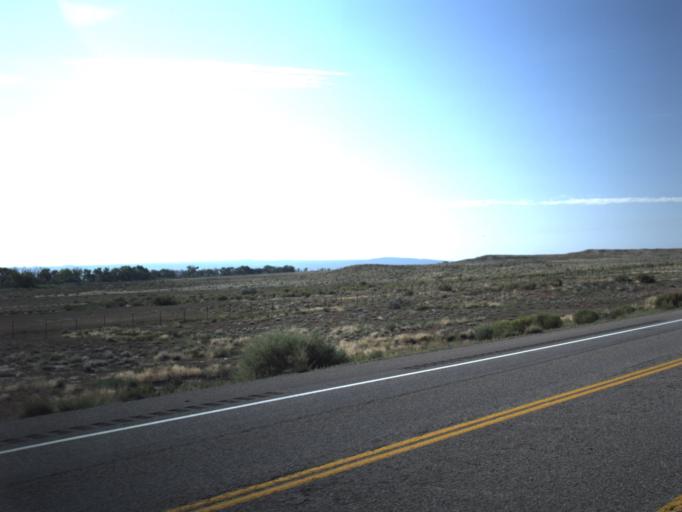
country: US
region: Utah
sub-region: Emery County
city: Huntington
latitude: 39.4311
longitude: -110.8682
